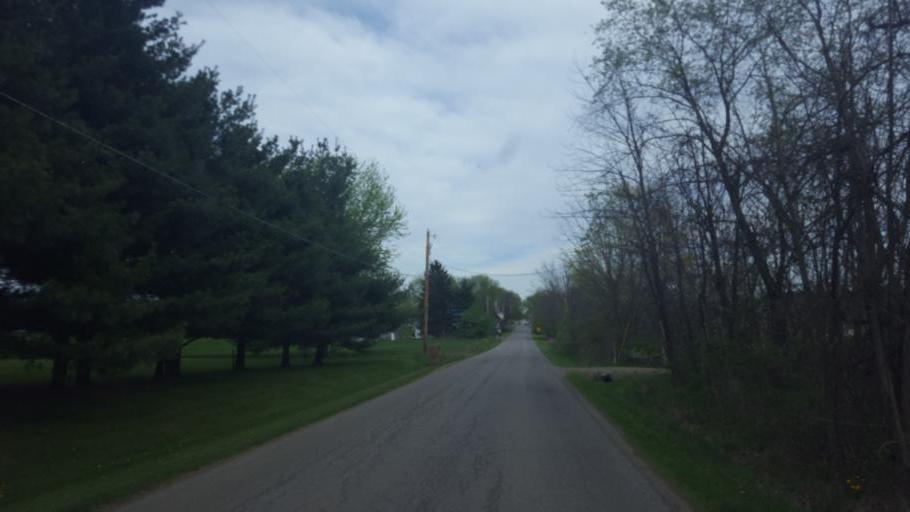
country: US
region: Ohio
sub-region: Richland County
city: Lexington
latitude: 40.6811
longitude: -82.6684
